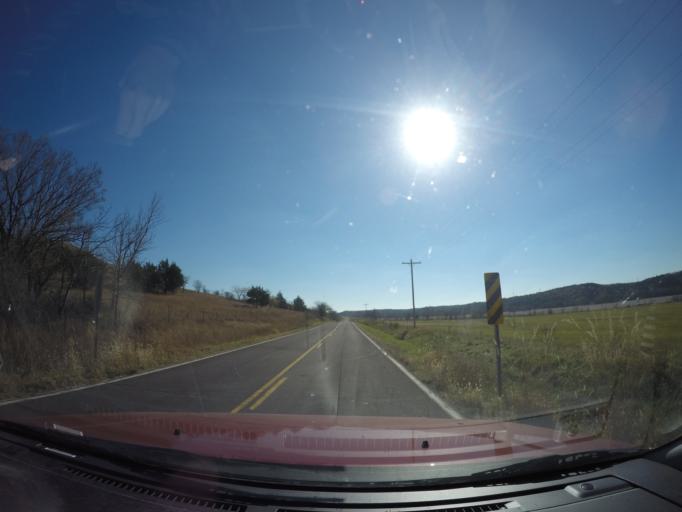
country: US
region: Kansas
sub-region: Geary County
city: Grandview Plaza
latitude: 38.9927
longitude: -96.7291
